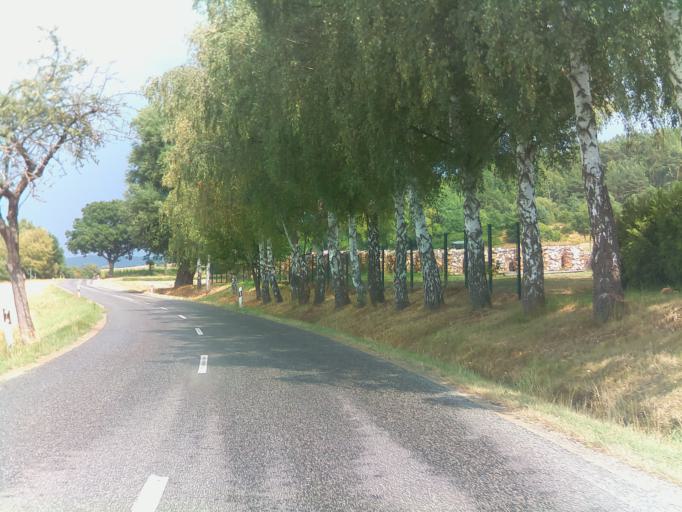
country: DE
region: Hesse
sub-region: Regierungsbezirk Kassel
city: Niederaula
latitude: 50.7955
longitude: 9.6232
